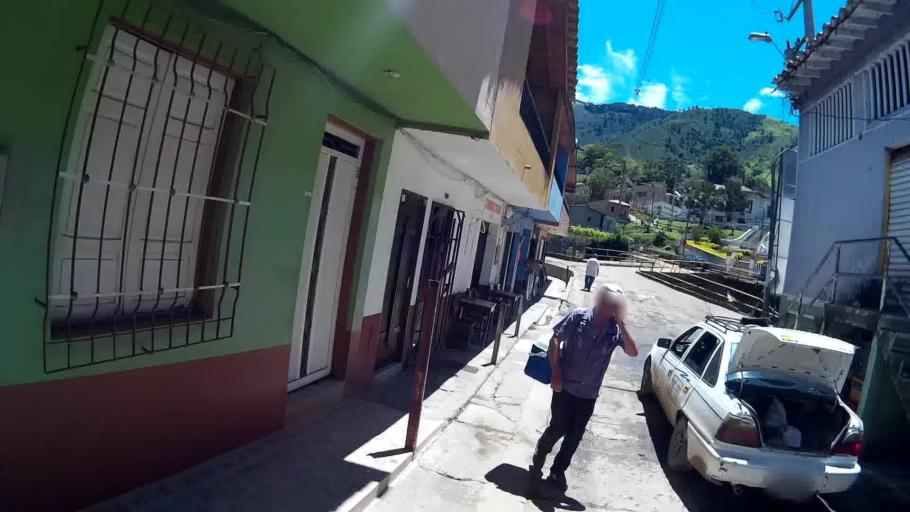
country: CO
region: Antioquia
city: Salgar
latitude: 5.9644
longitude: -75.9802
